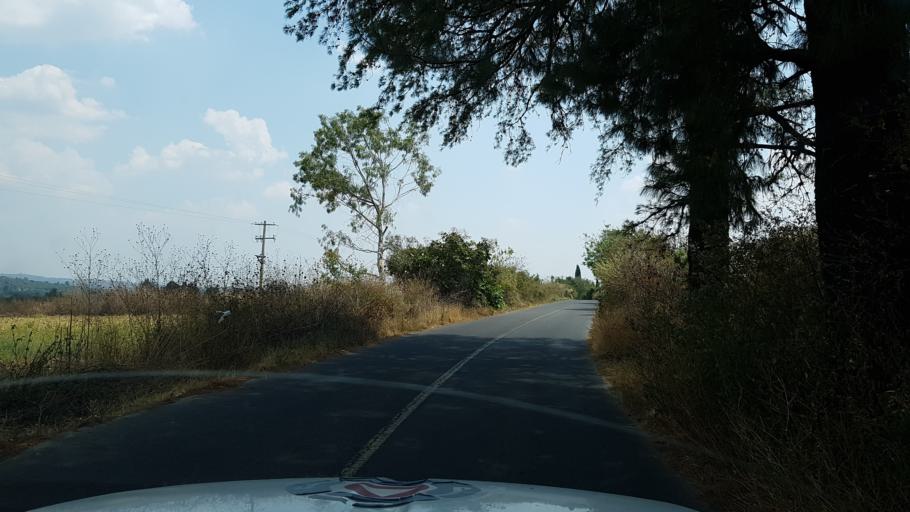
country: MX
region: Morelos
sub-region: Yecapixtla
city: Texcala
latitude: 18.9211
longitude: -98.8077
